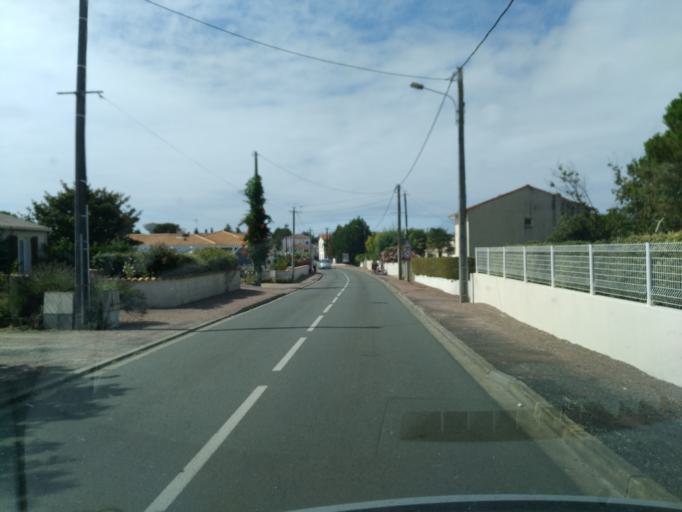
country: FR
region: Poitou-Charentes
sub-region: Departement de la Charente-Maritime
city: Saint-Palais-sur-Mer
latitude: 45.6585
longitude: -1.0760
